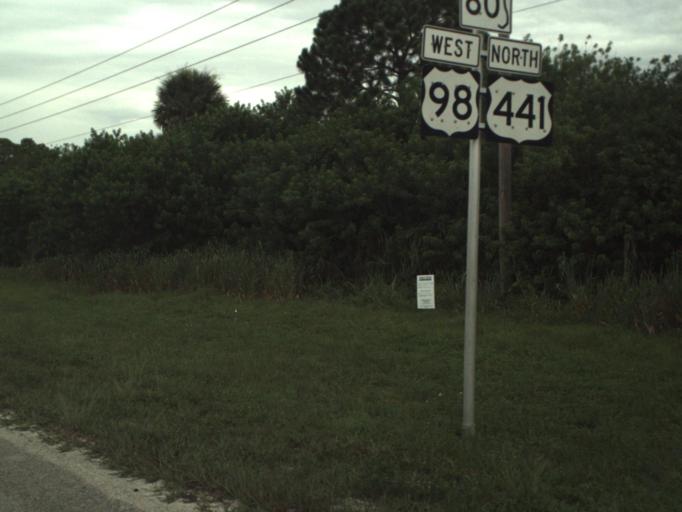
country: US
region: Florida
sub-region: Palm Beach County
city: Loxahatchee Groves
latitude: 26.6832
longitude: -80.2920
